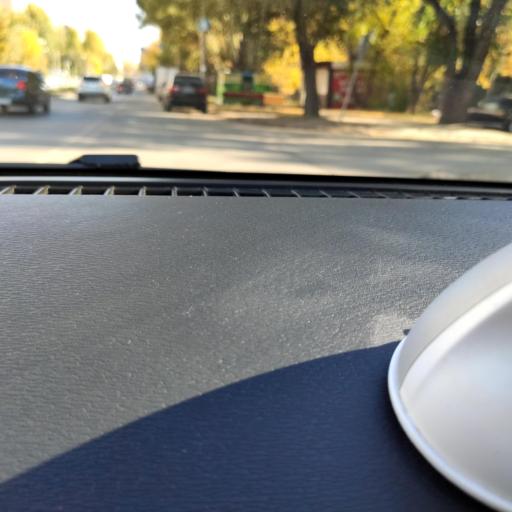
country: RU
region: Samara
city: Samara
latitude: 53.2286
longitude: 50.2470
